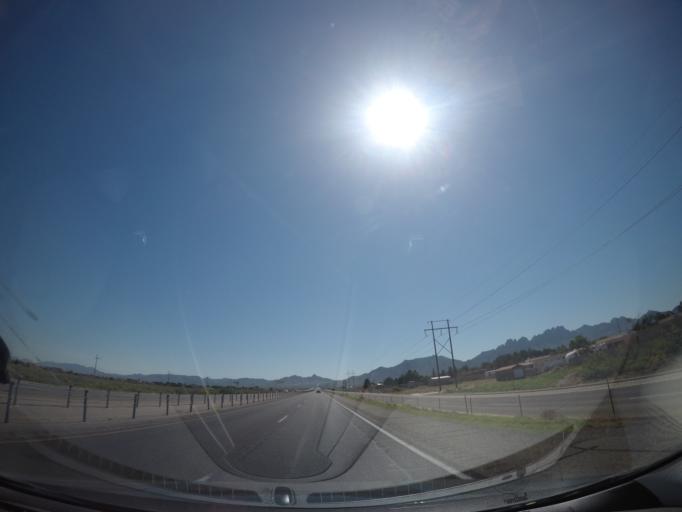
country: US
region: New Mexico
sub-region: Dona Ana County
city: Las Cruces
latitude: 32.3926
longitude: -106.6931
